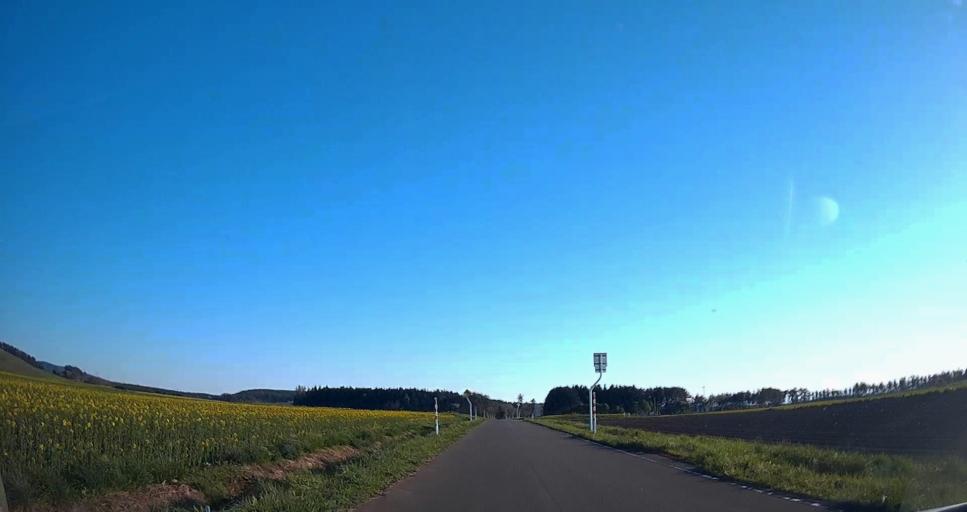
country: JP
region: Aomori
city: Mutsu
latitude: 41.1152
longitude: 141.2739
